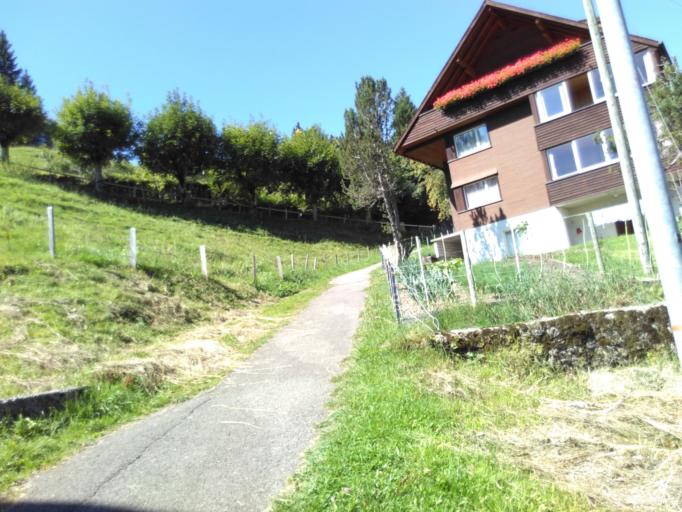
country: CH
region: Lucerne
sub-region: Lucerne-Land District
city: Vitznau
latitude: 47.0433
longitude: 8.4864
